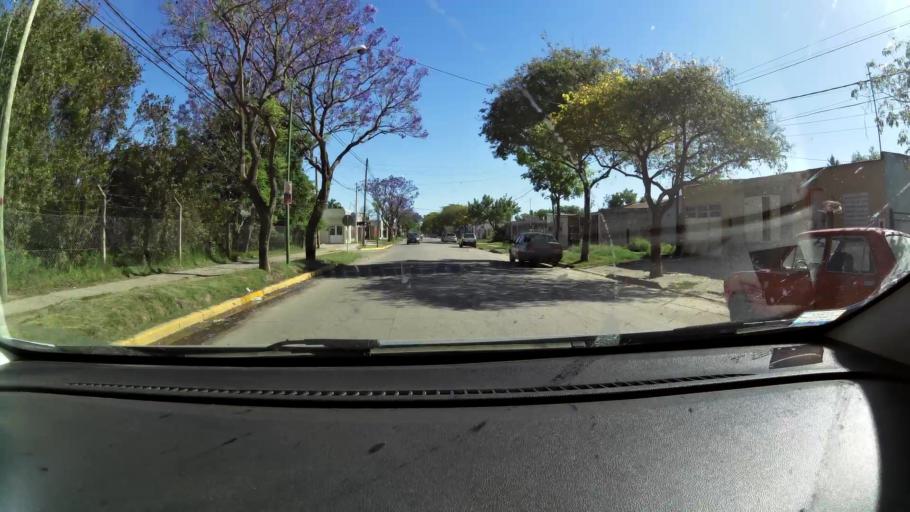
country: AR
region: Santa Fe
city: Rafaela
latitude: -31.2370
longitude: -61.4739
